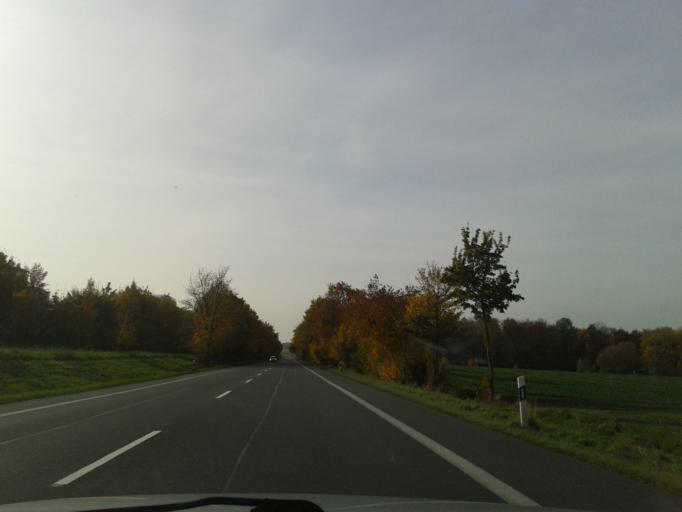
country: DE
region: North Rhine-Westphalia
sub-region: Regierungsbezirk Detmold
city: Buren
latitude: 51.5614
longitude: 8.5289
